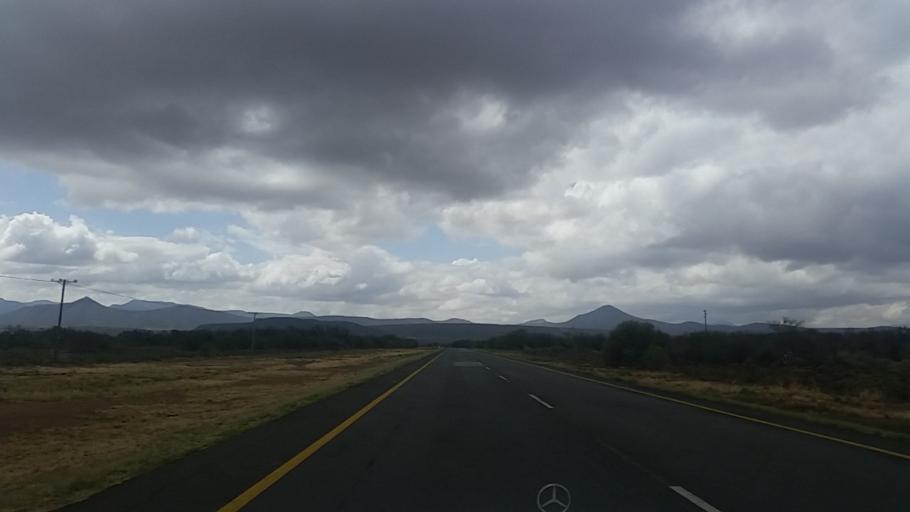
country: ZA
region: Eastern Cape
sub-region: Cacadu District Municipality
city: Graaff-Reinet
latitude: -32.1818
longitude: 24.5621
